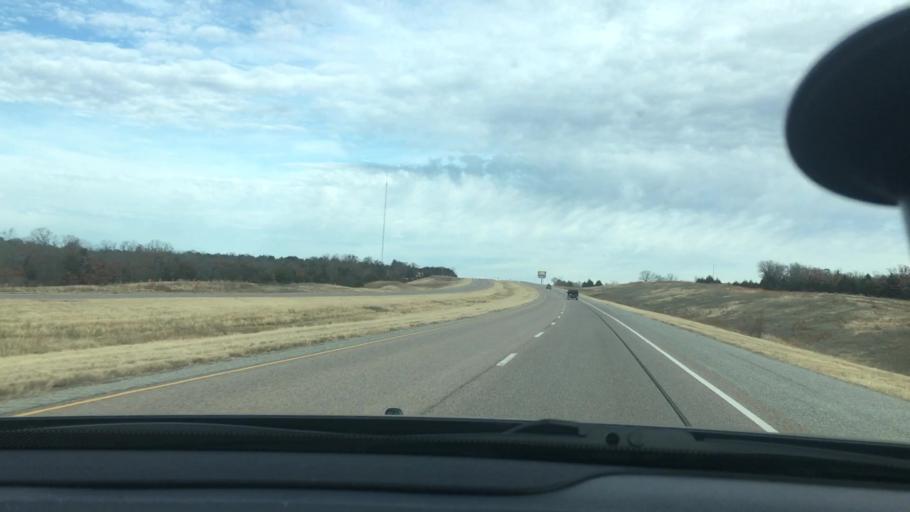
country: US
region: Oklahoma
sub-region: Pontotoc County
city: Byng
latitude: 34.8848
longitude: -96.6754
